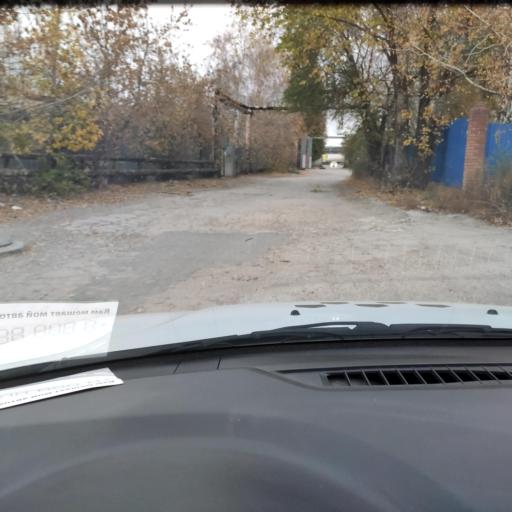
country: RU
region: Samara
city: Tol'yatti
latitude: 53.5312
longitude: 49.4518
